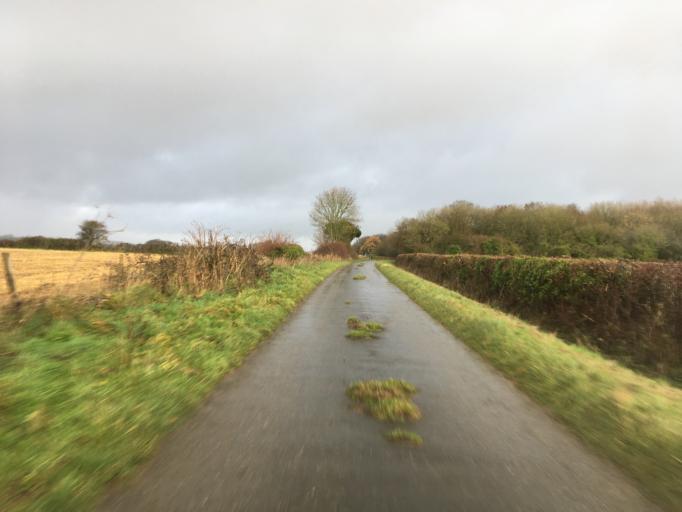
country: GB
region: England
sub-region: Wiltshire
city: Hankerton
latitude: 51.6499
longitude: -2.0698
